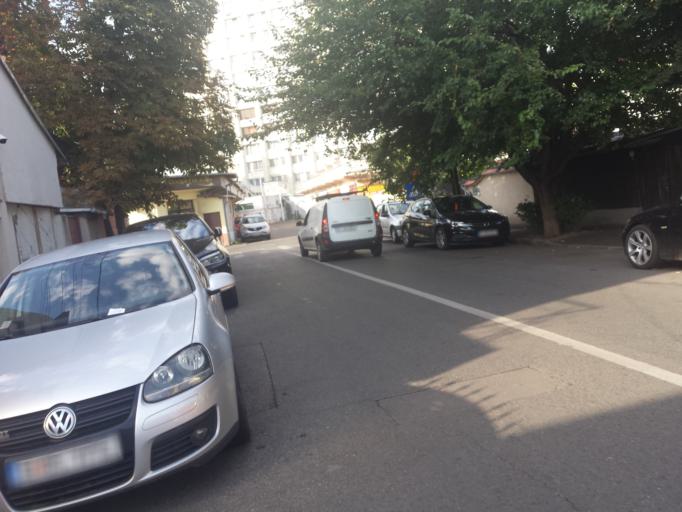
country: RO
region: Ilfov
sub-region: Comuna Chiajna
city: Rosu
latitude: 44.4636
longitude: 26.0578
